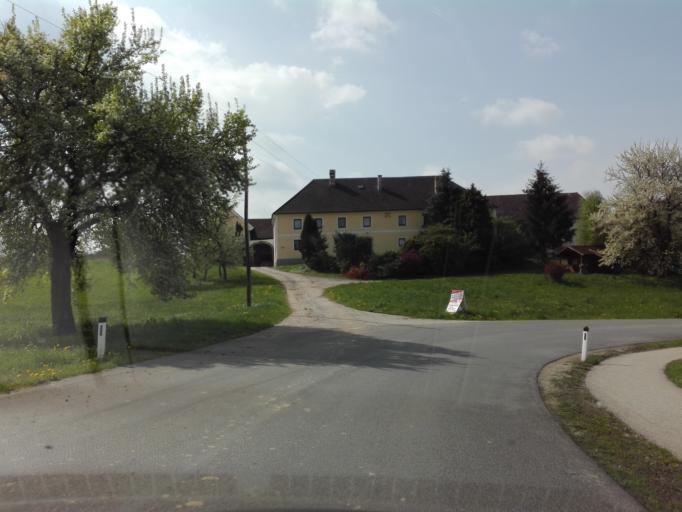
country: AT
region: Upper Austria
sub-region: Politischer Bezirk Perg
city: Perg
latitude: 48.2636
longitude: 14.7096
